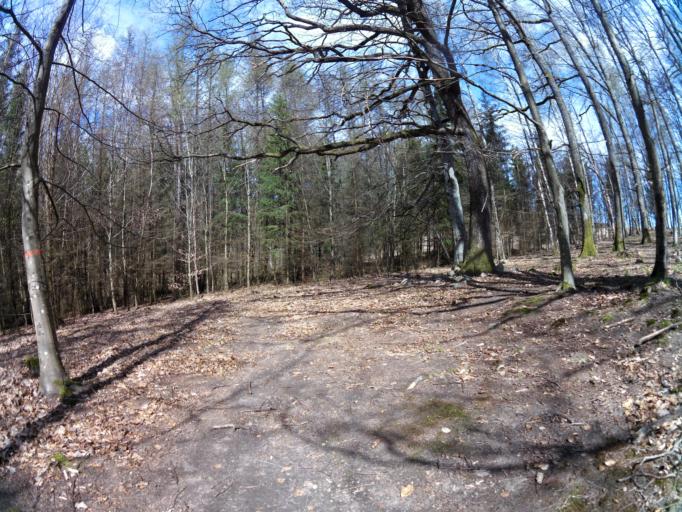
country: PL
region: West Pomeranian Voivodeship
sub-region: Powiat szczecinecki
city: Szczecinek
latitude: 53.7834
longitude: 16.6187
